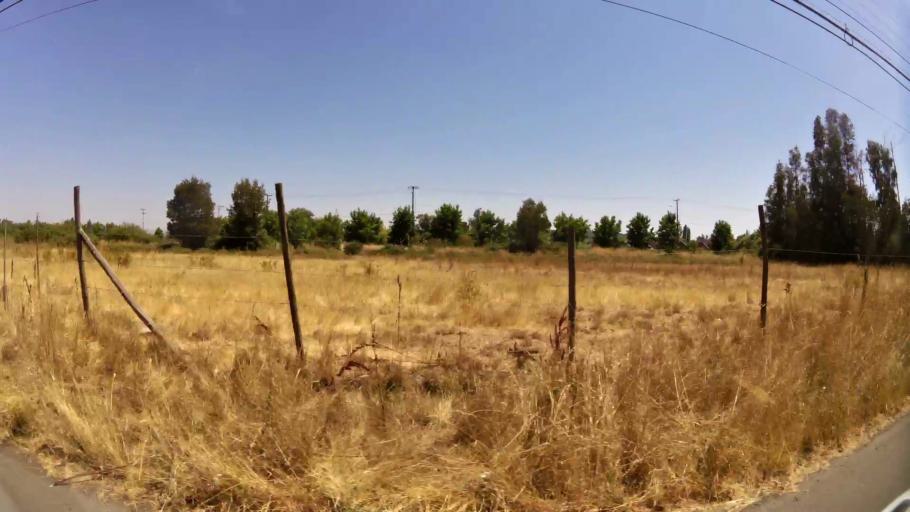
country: CL
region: Maule
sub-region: Provincia de Curico
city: Curico
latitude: -34.9937
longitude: -71.2114
